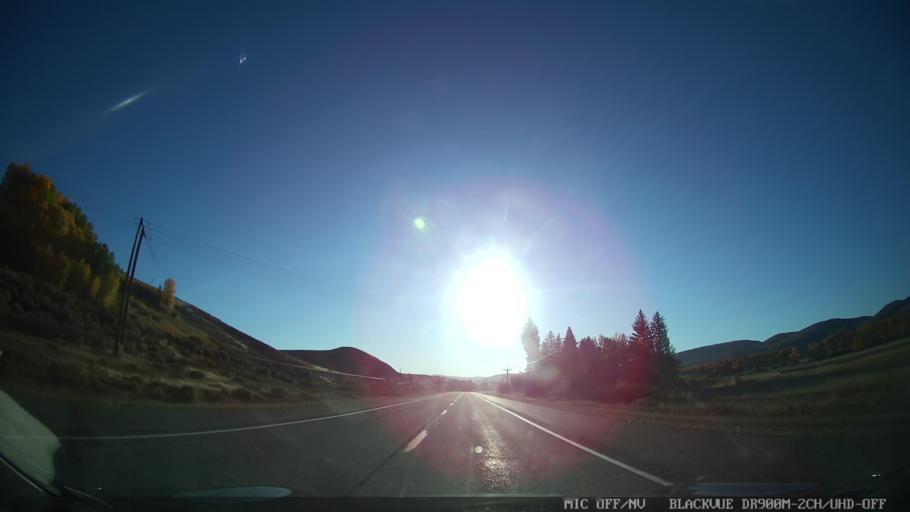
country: US
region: Colorado
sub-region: Grand County
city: Kremmling
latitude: 40.0672
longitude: -106.2629
